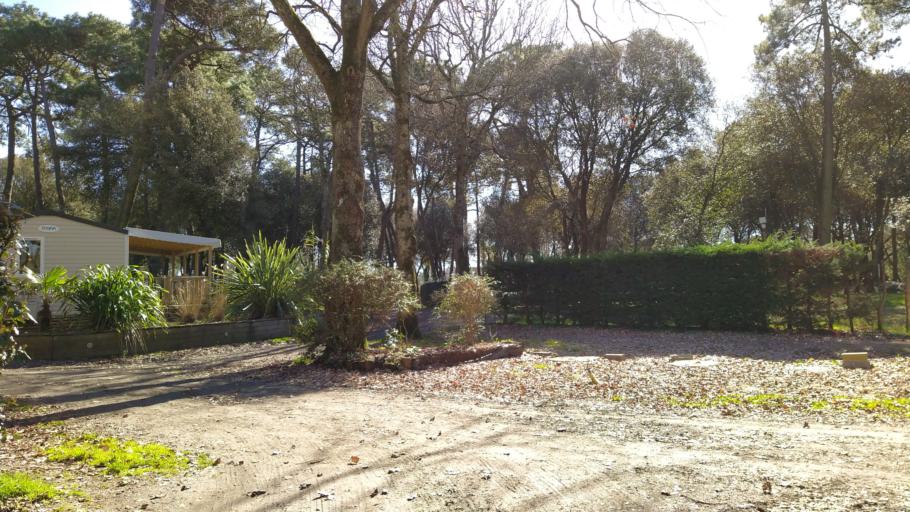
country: FR
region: Pays de la Loire
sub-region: Departement de la Loire-Atlantique
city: Saint-Michel-Chef-Chef
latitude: 47.2132
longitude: -2.1569
